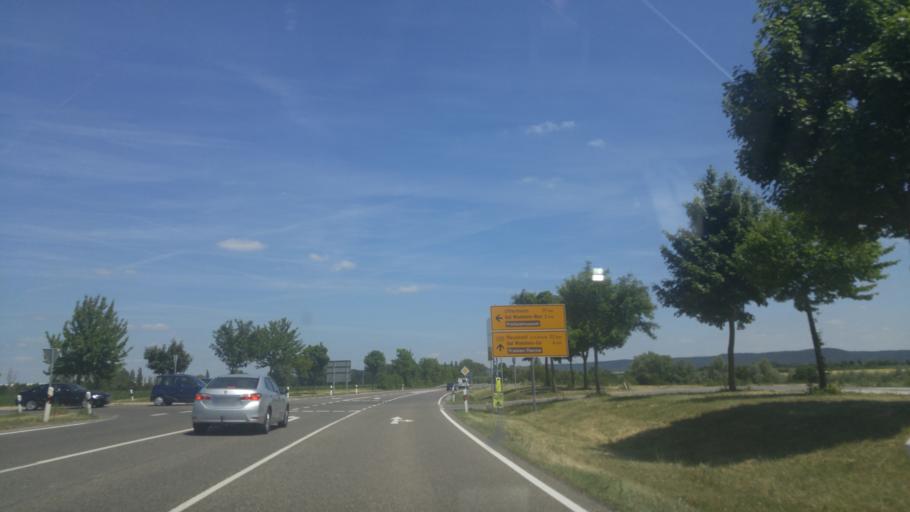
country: DE
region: Bavaria
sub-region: Regierungsbezirk Mittelfranken
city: Bad Windsheim
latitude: 49.4900
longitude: 10.3943
